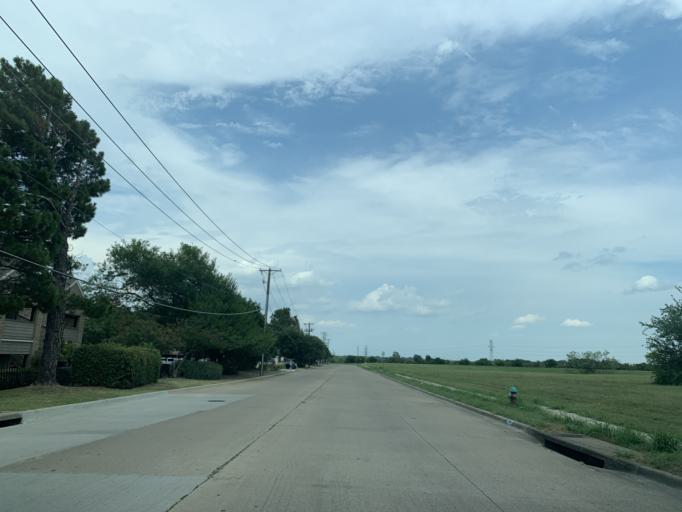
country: US
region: Texas
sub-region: Tarrant County
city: Watauga
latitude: 32.8341
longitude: -97.2706
